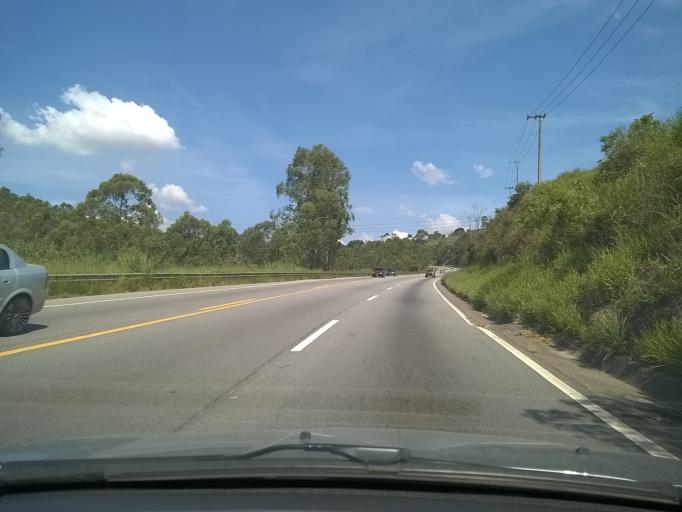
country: BR
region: Sao Paulo
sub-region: Francisco Morato
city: Francisco Morato
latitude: -23.2949
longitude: -46.7871
